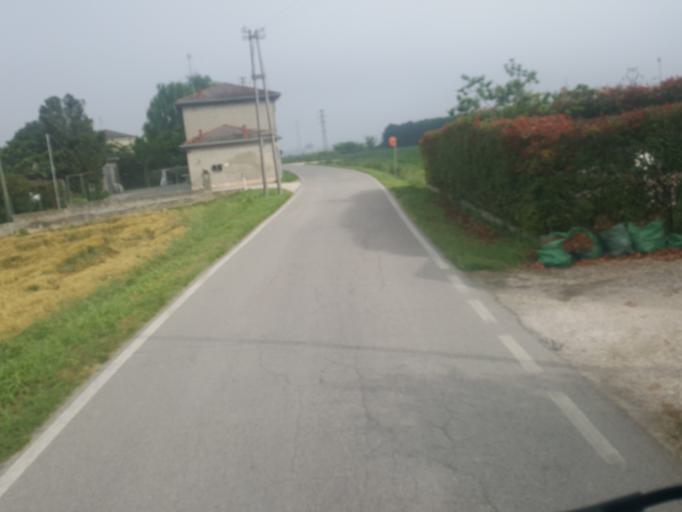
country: IT
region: Veneto
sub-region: Provincia di Rovigo
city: Canaro
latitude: 44.9372
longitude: 11.6490
